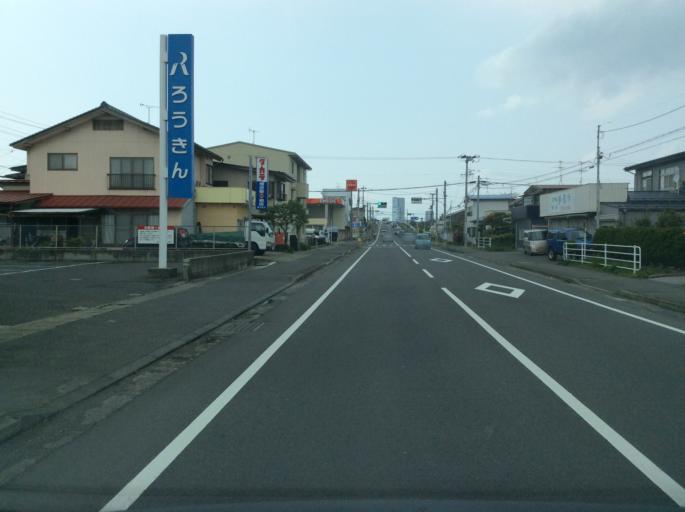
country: JP
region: Fukushima
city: Koriyama
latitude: 37.3839
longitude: 140.4042
